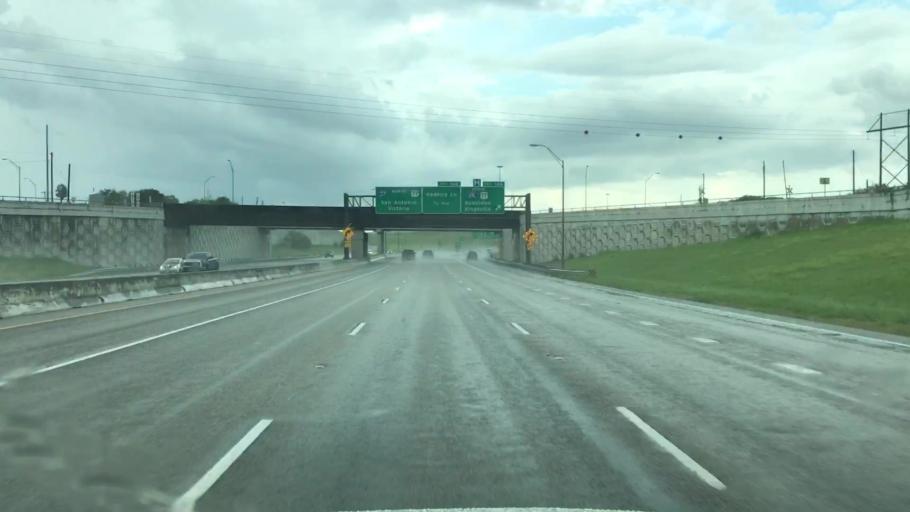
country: US
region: Texas
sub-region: Nueces County
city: Robstown
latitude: 27.8615
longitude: -97.6155
